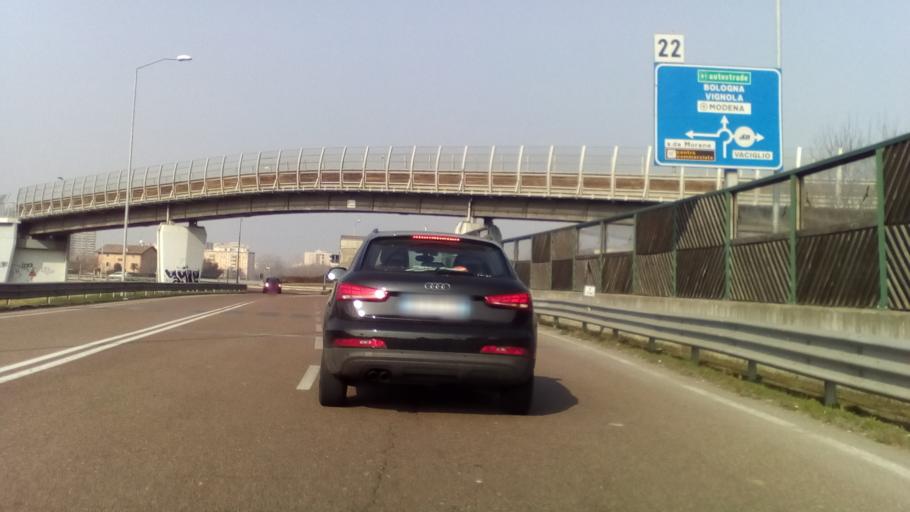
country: IT
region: Emilia-Romagna
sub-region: Provincia di Modena
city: Modena
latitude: 44.6126
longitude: 10.9367
